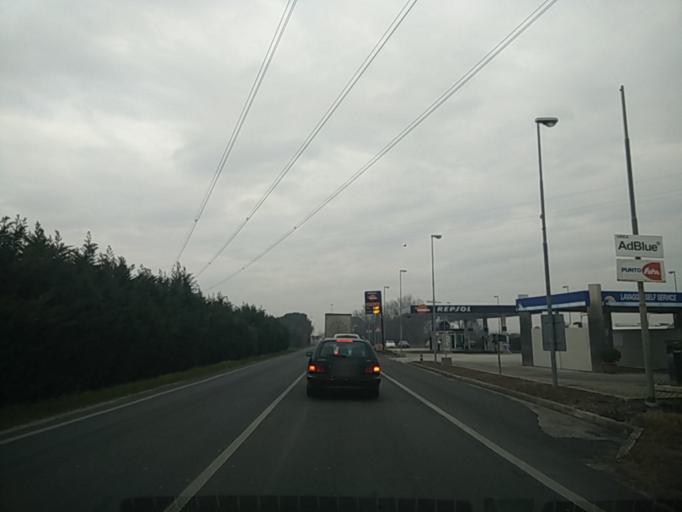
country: IT
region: Emilia-Romagna
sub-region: Provincia di Rimini
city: Santa Giustina
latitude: 44.0767
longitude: 12.4647
